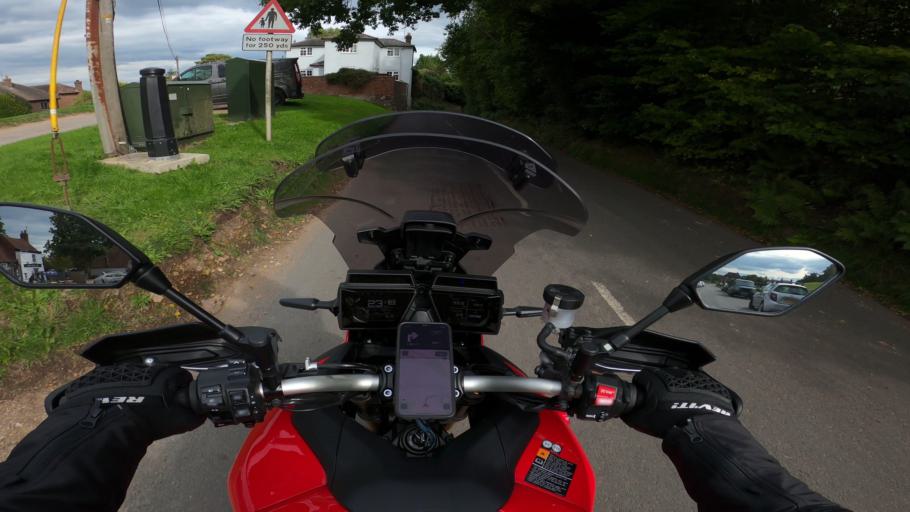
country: GB
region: England
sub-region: Kent
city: Westerham
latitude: 51.2462
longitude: 0.1290
